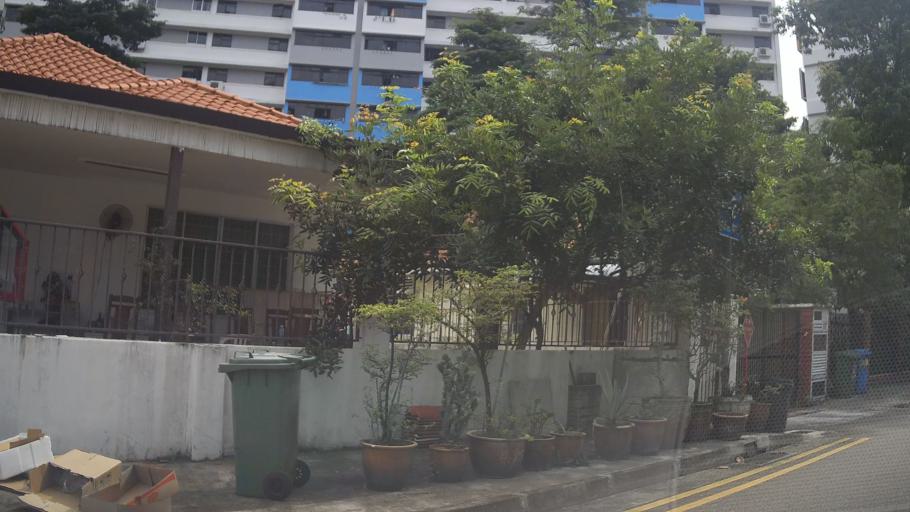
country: SG
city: Singapore
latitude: 1.3242
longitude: 103.8659
